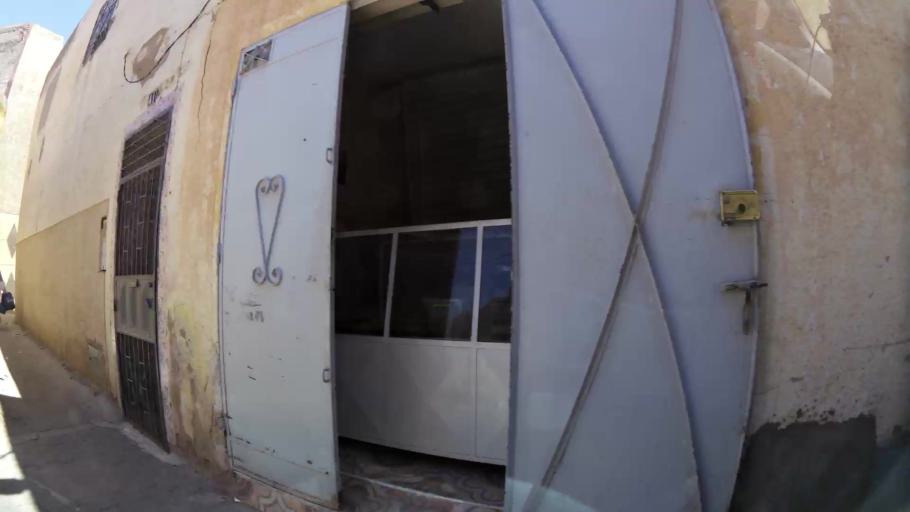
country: MA
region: Oriental
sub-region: Oujda-Angad
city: Oujda
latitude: 34.6726
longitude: -1.9281
